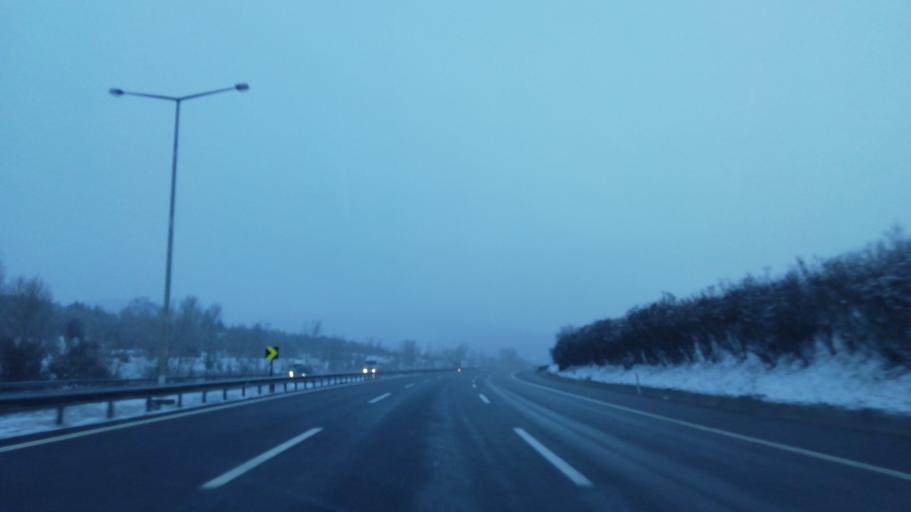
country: TR
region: Bolu
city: Bolu
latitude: 40.7497
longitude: 31.5627
